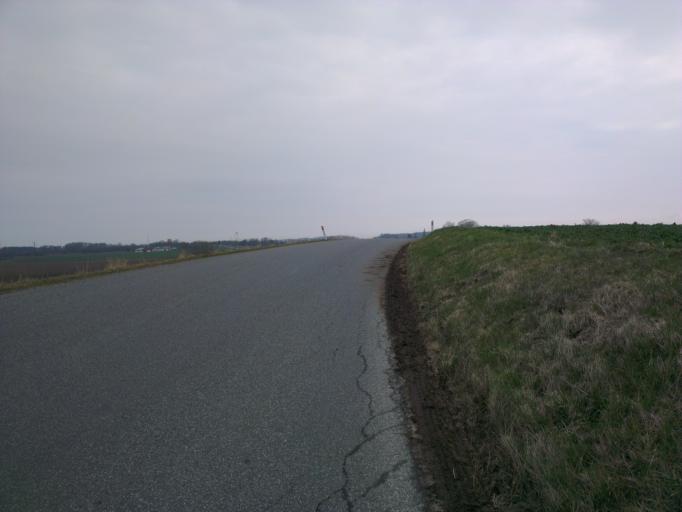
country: DK
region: Capital Region
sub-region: Frederikssund Kommune
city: Skibby
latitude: 55.7486
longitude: 11.9033
